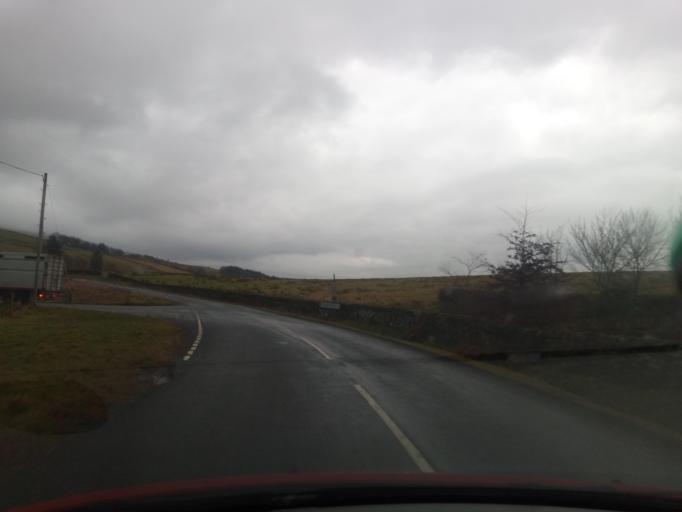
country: GB
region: Scotland
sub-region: The Scottish Borders
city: Hawick
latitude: 55.2631
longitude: -2.6921
